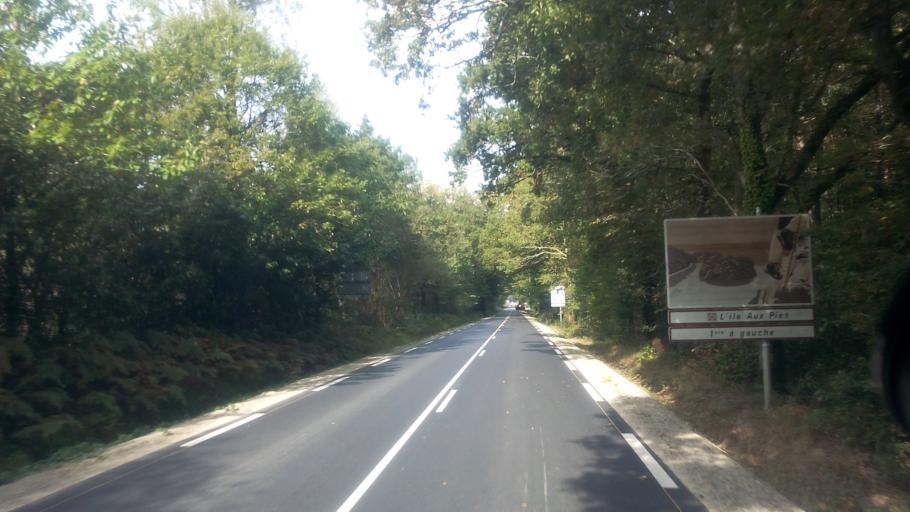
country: FR
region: Brittany
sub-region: Departement d'Ille-et-Vilaine
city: Bains-sur-Oust
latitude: 47.7058
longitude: -2.0867
